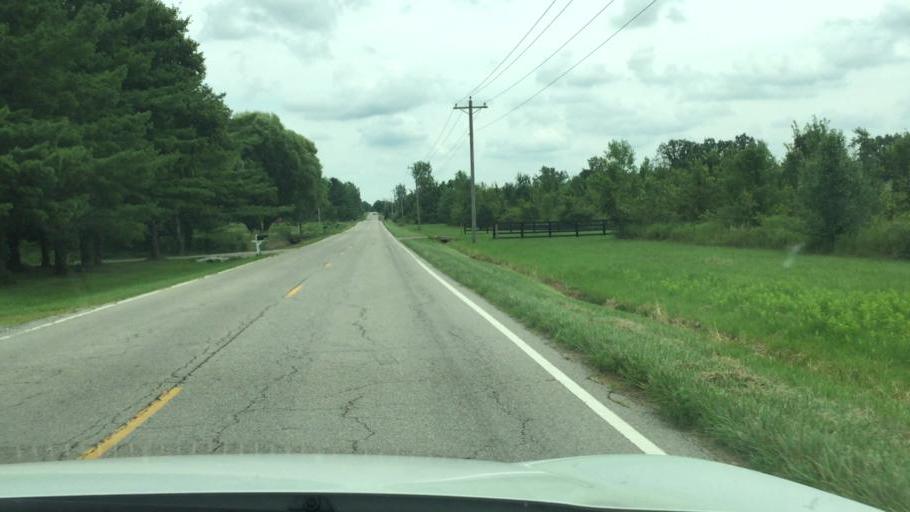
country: US
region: Ohio
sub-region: Champaign County
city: North Lewisburg
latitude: 40.2510
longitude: -83.4849
